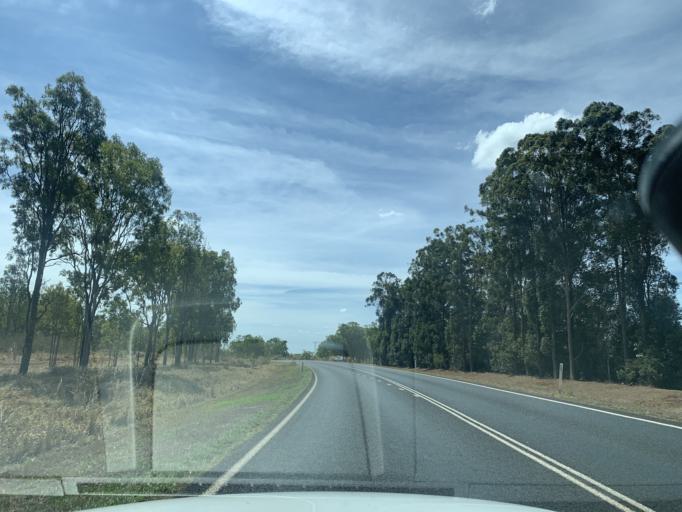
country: AU
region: Queensland
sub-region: Tablelands
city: Tolga
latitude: -17.1845
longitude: 145.4648
